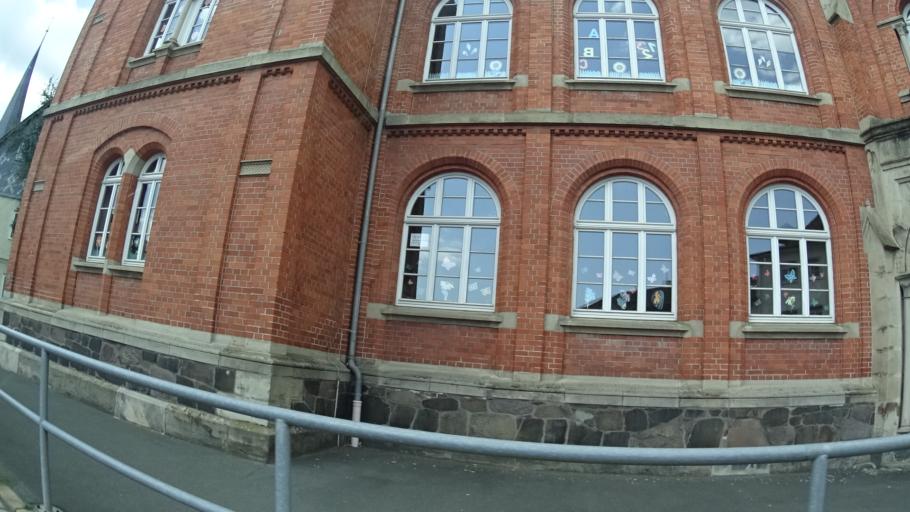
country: DE
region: Thuringia
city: Sonneberg
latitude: 50.3413
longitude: 11.1816
